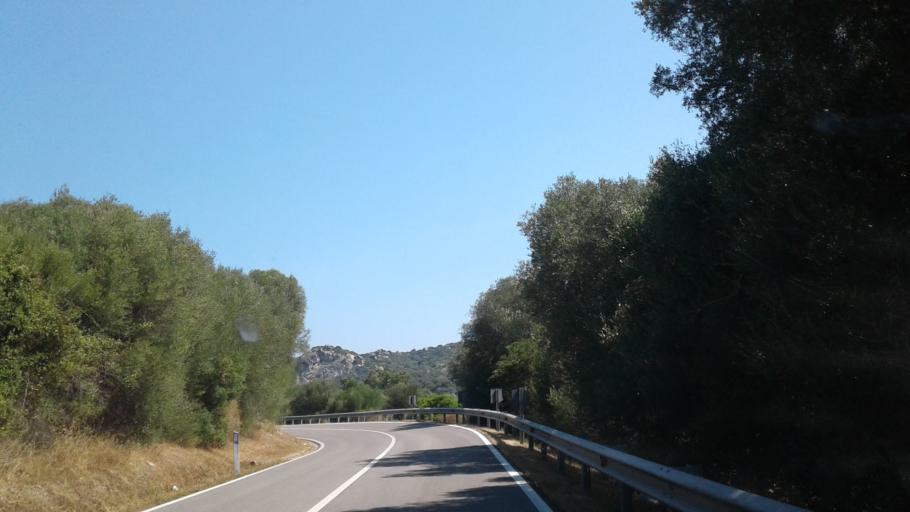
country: IT
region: Sardinia
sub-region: Provincia di Olbia-Tempio
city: Palau
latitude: 41.1500
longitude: 9.3138
